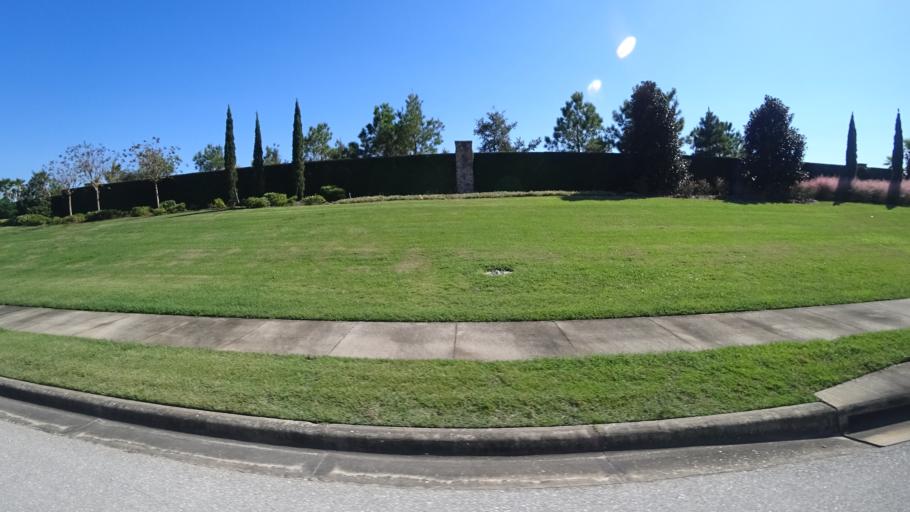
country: US
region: Florida
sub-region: Sarasota County
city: The Meadows
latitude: 27.4011
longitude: -82.3817
